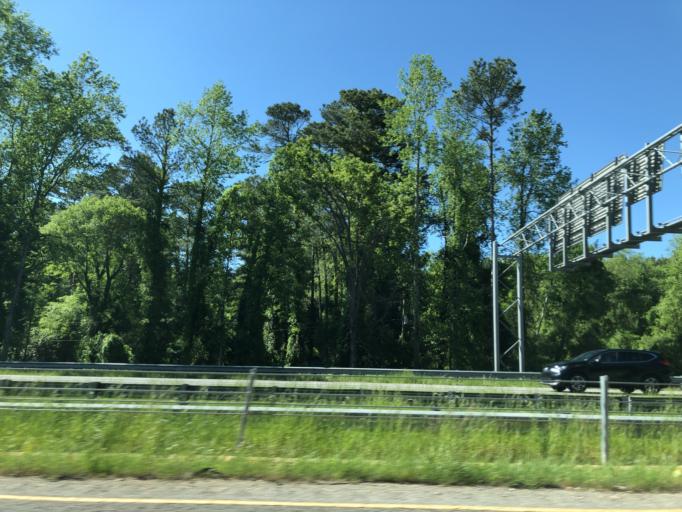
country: US
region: Georgia
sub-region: Clarke County
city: Country Club Estates
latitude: 33.9656
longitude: -83.4259
